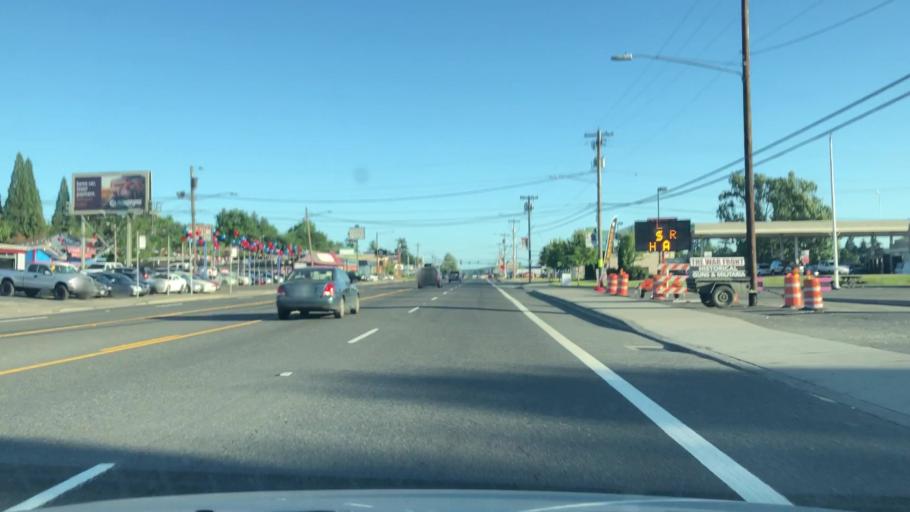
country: US
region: Oregon
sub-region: Clackamas County
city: Oak Grove
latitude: 45.4256
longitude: -122.6340
